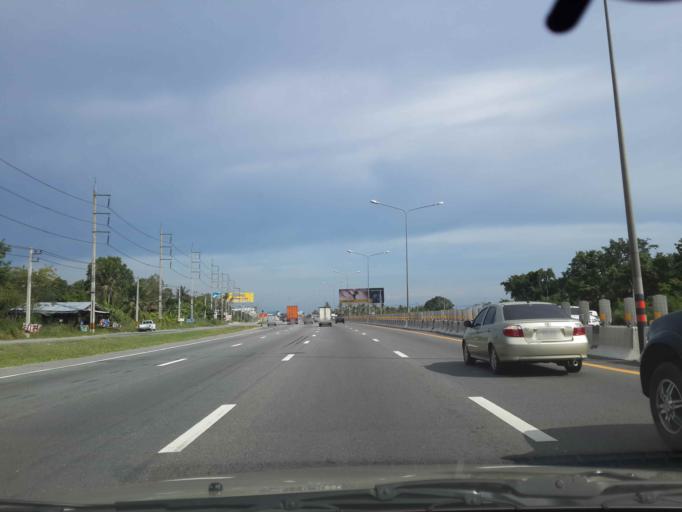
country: TH
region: Chon Buri
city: Si Racha
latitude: 13.2585
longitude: 100.9902
